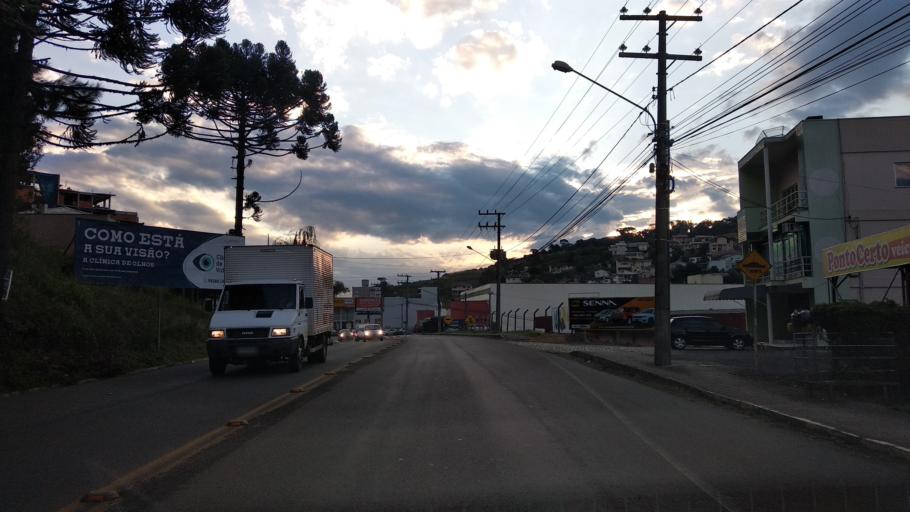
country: BR
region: Santa Catarina
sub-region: Videira
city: Videira
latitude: -27.0028
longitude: -51.1338
